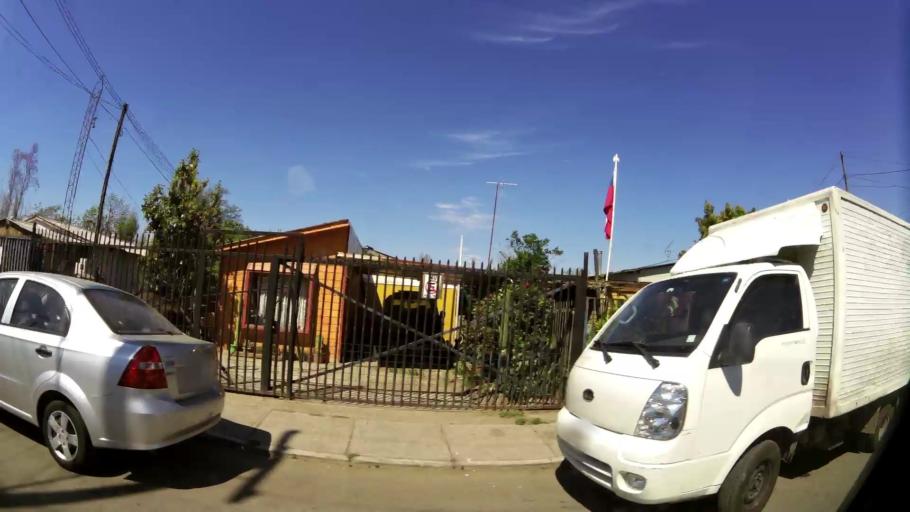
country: CL
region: Santiago Metropolitan
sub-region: Provincia de Talagante
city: Penaflor
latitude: -33.6016
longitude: -70.8810
